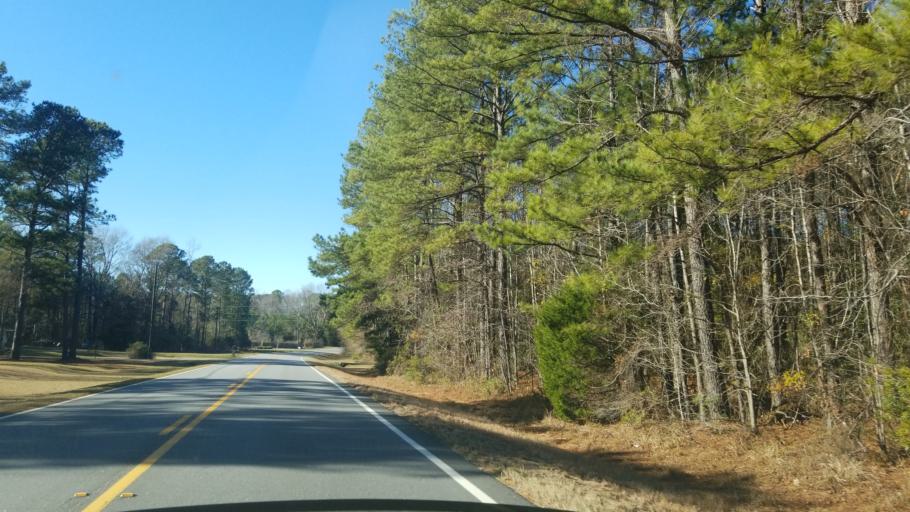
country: US
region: Georgia
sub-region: Harris County
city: Hamilton
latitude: 32.6700
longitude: -84.9019
